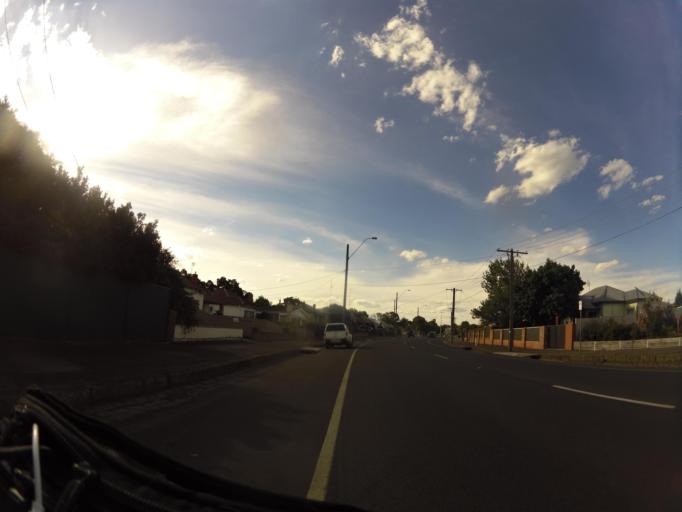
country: AU
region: Victoria
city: Ballarat East
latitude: -37.5685
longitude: 143.8692
